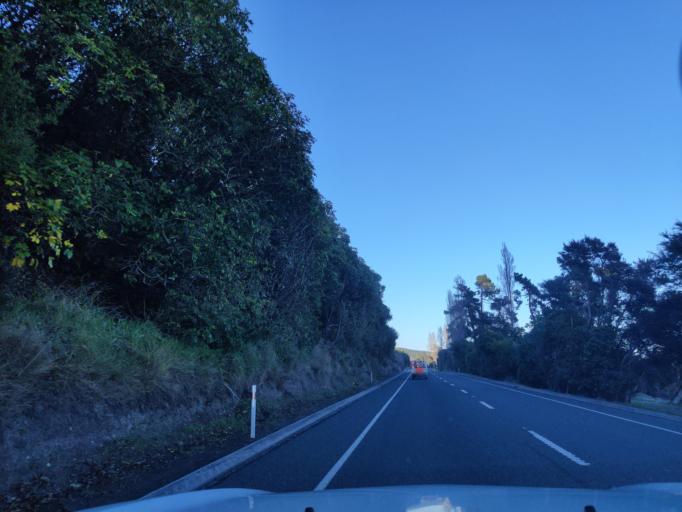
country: NZ
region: Waikato
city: Turangi
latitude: -38.8917
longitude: 175.9498
